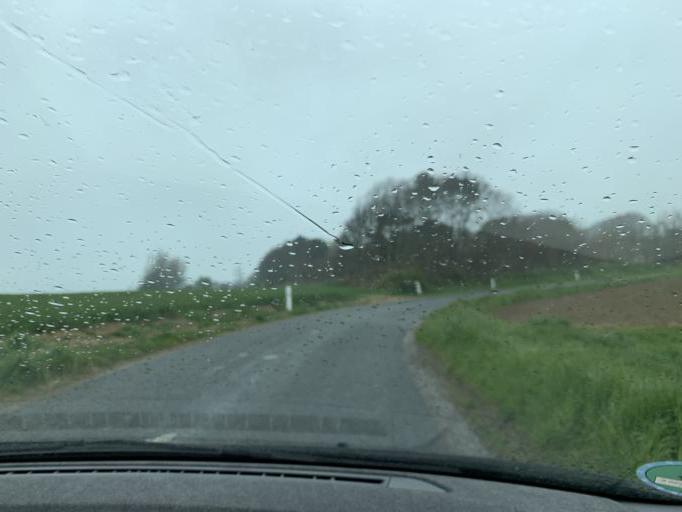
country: FR
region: Haute-Normandie
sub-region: Departement de la Seine-Maritime
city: Etretat
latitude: 49.7137
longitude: 0.2382
